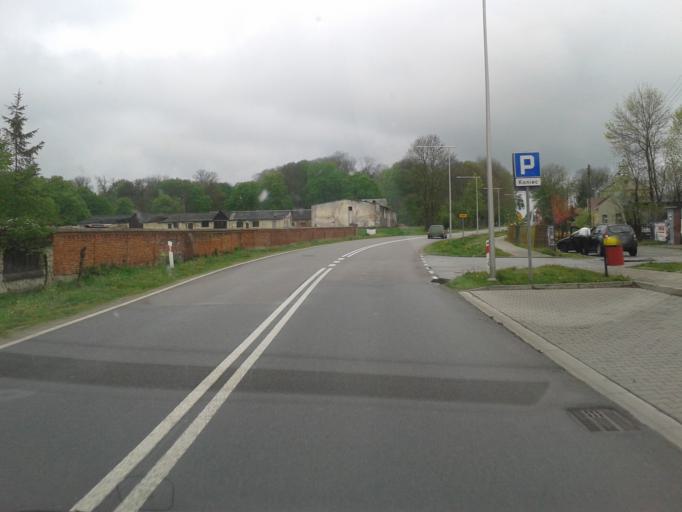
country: PL
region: Lublin Voivodeship
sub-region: Powiat hrubieszowski
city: Dolhobyczow
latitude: 50.5864
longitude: 24.0335
